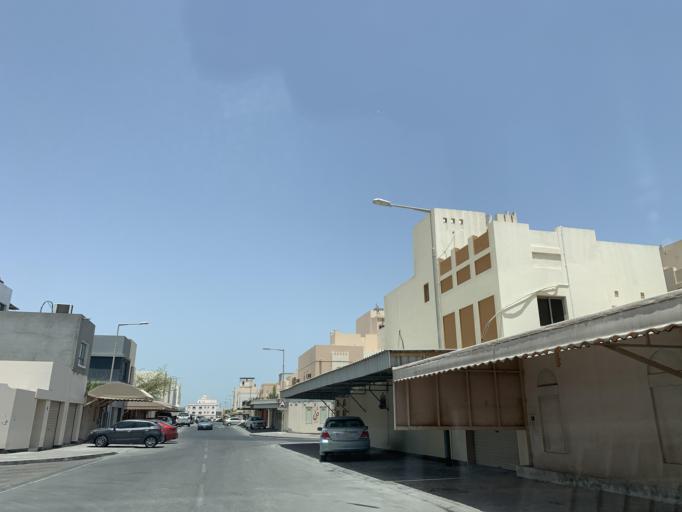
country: BH
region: Northern
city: Sitrah
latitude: 26.1391
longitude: 50.5914
